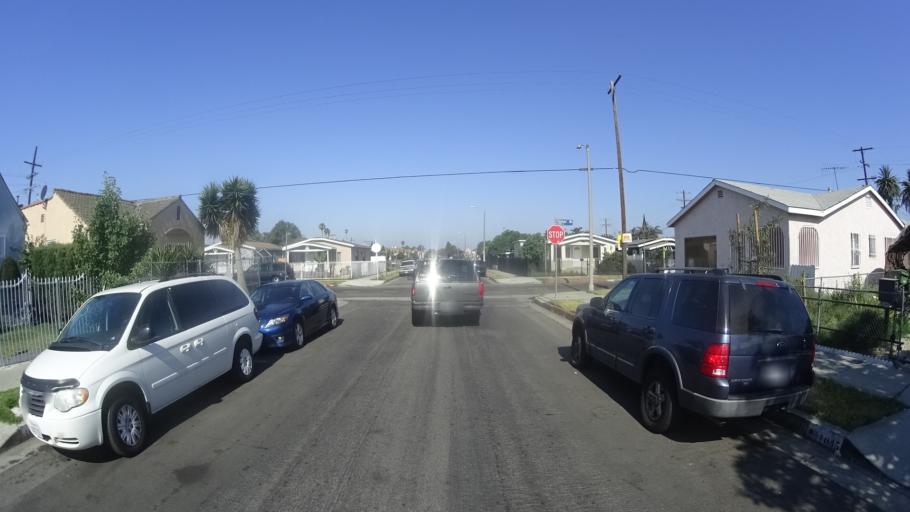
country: US
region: California
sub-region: Los Angeles County
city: Westmont
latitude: 33.9798
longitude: -118.2934
